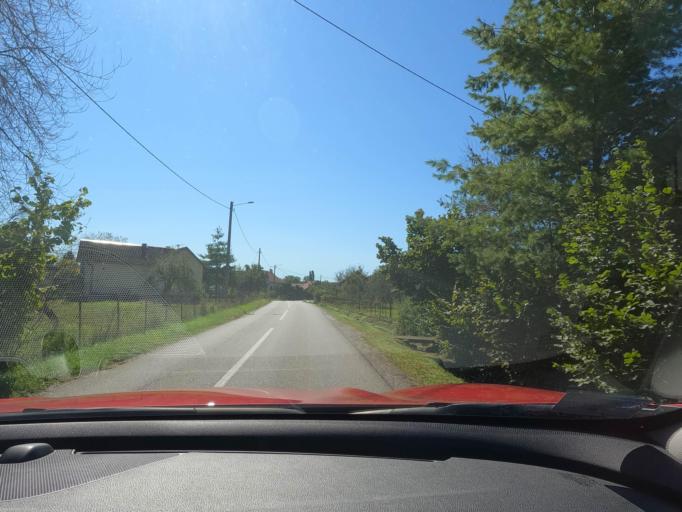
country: HR
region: Sisacko-Moslavacka
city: Petrinja
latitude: 45.4769
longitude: 16.3201
